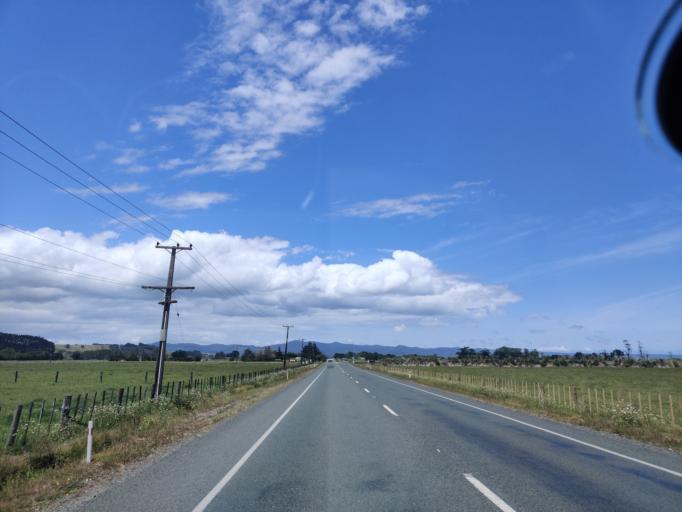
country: NZ
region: Northland
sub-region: Far North District
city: Kaitaia
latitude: -35.0486
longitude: 173.2567
